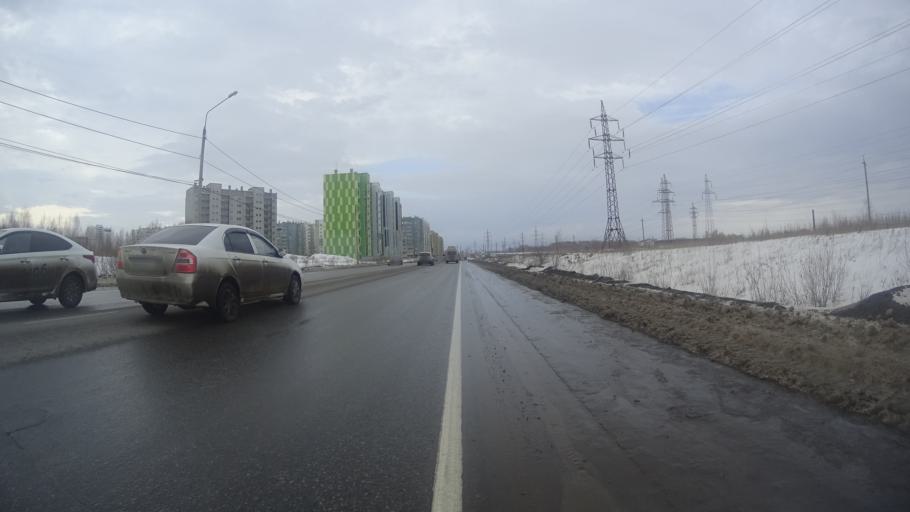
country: RU
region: Chelyabinsk
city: Roshchino
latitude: 55.2123
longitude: 61.3081
